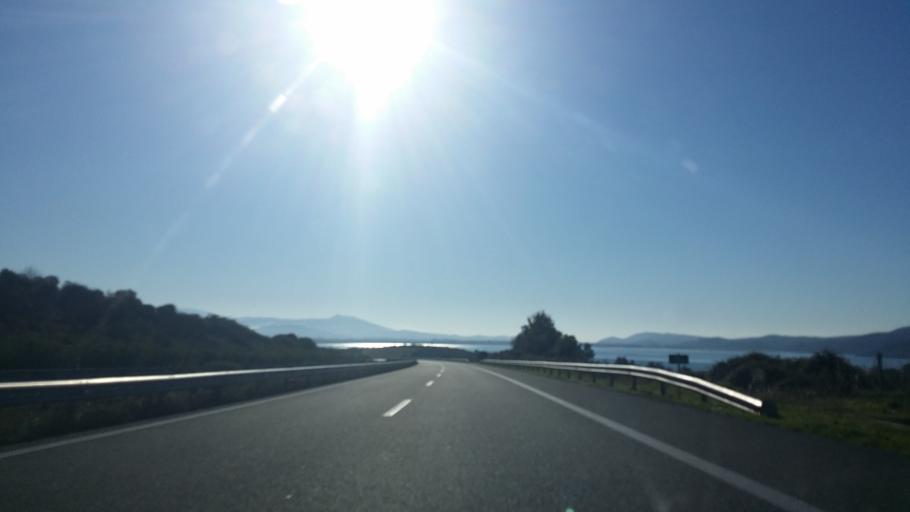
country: GR
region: West Greece
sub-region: Nomos Aitolias kai Akarnanias
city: Fitiai
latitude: 38.6841
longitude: 21.2170
